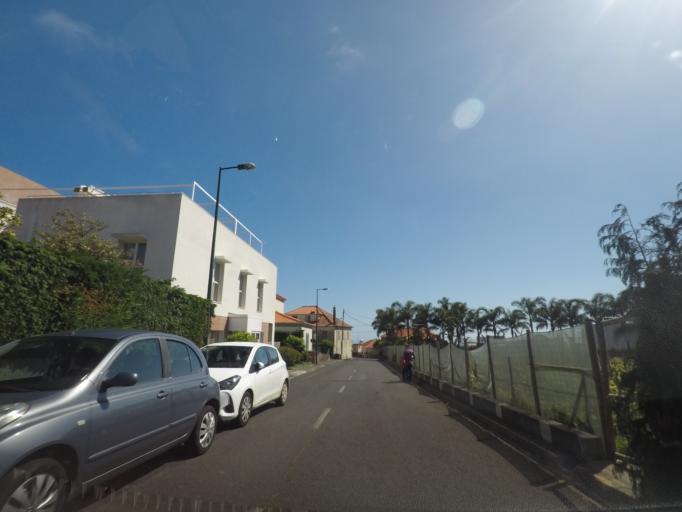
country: PT
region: Madeira
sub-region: Calheta
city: Arco da Calheta
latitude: 32.6980
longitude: -17.1180
